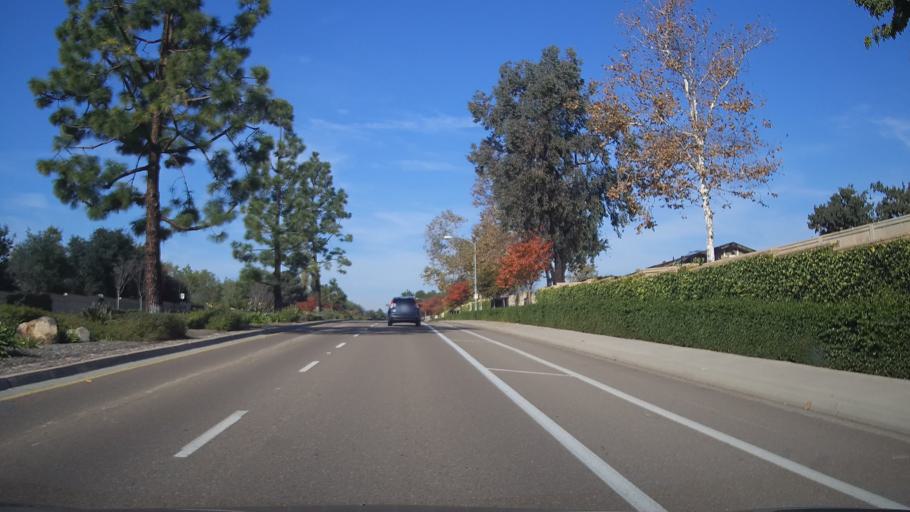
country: US
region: California
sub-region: San Diego County
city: La Mesa
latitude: 32.8105
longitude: -117.1054
